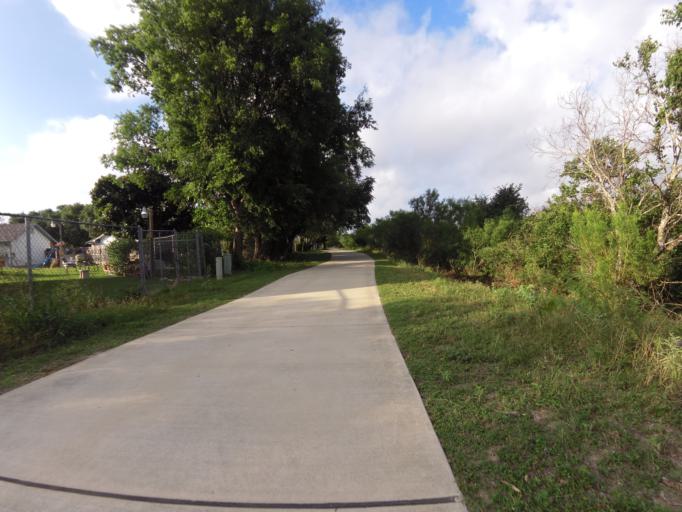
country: US
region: Texas
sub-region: Bexar County
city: Leon Valley
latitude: 29.4961
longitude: -98.6369
